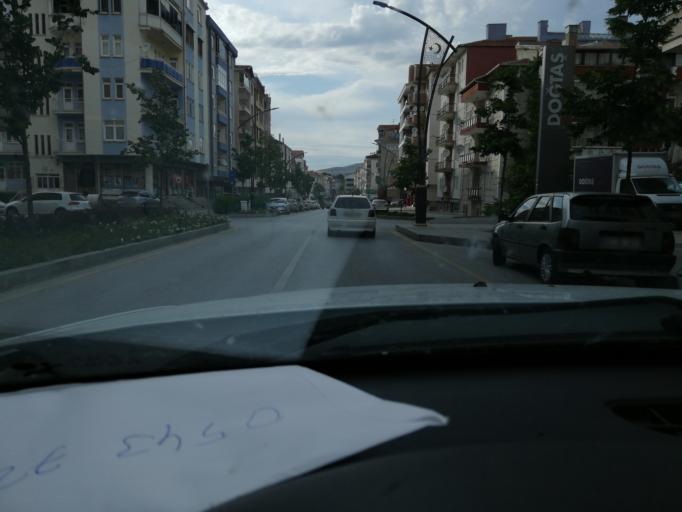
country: TR
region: Kirsehir
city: Kirsehir
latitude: 39.1404
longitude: 34.1643
